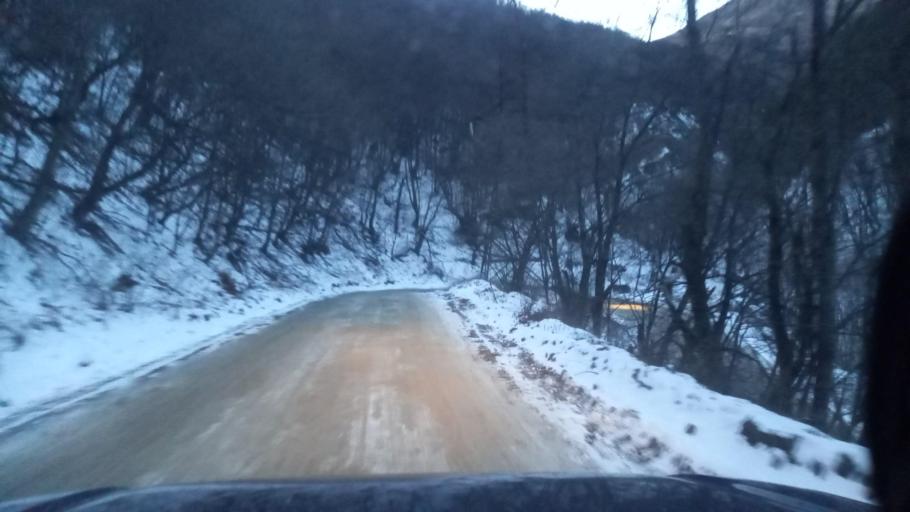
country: RU
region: Ingushetiya
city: Dzhayrakh
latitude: 42.8253
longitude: 44.5924
